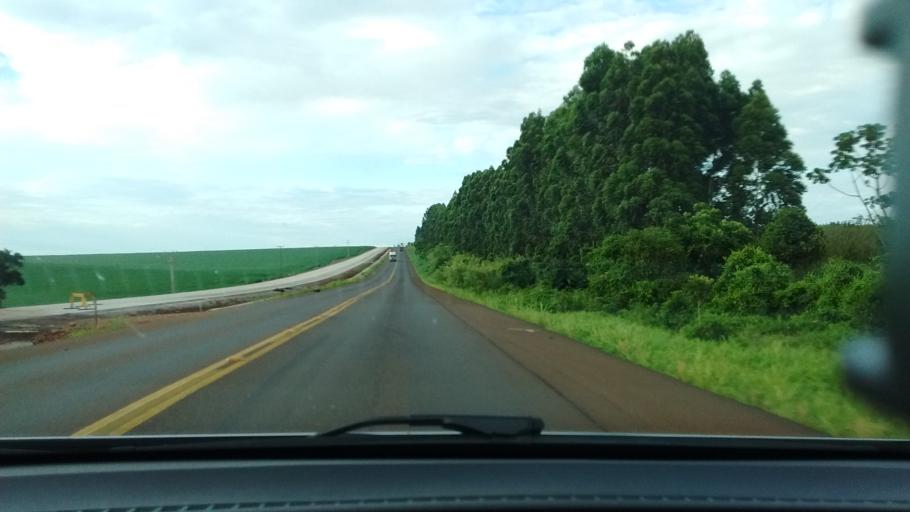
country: BR
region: Parana
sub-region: Cascavel
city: Cascavel
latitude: -25.0511
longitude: -53.5585
